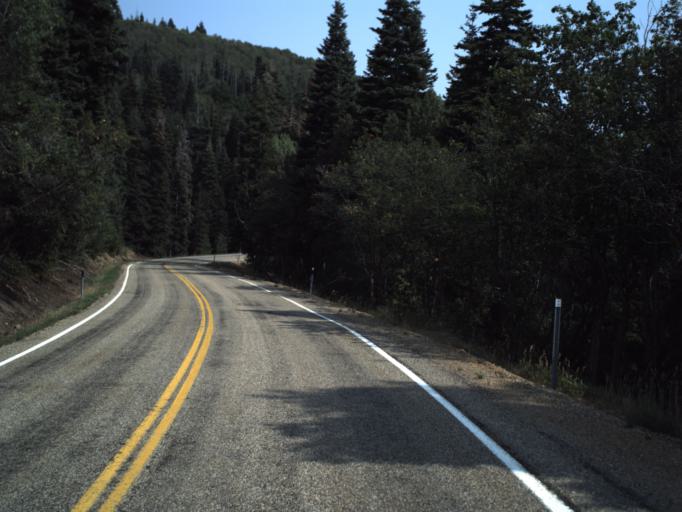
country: US
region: Utah
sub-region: Summit County
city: Summit Park
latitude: 40.8374
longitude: -111.6413
